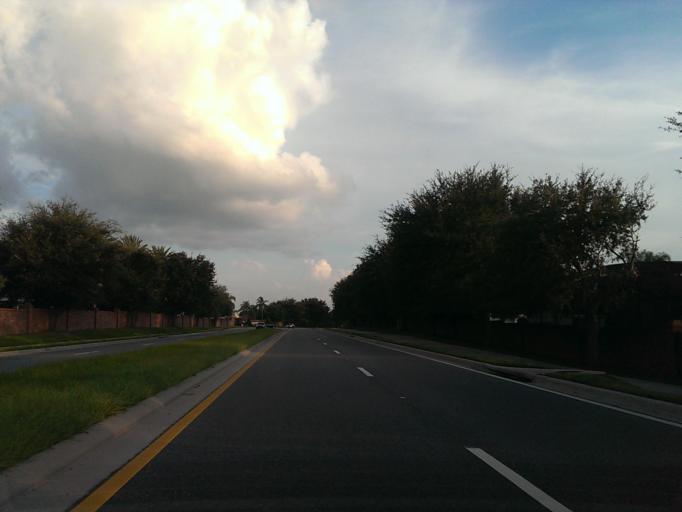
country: US
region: Florida
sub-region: Orange County
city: Lake Butler
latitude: 28.5136
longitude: -81.5845
